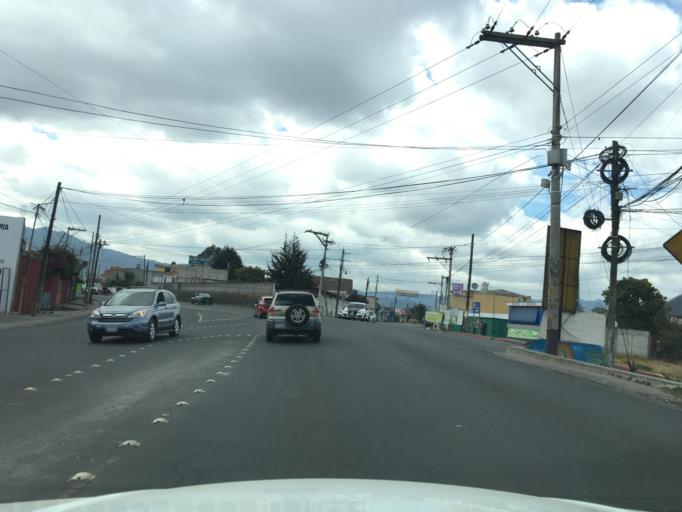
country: GT
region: Quetzaltenango
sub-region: Municipio de La Esperanza
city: La Esperanza
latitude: 14.8682
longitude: -91.5728
